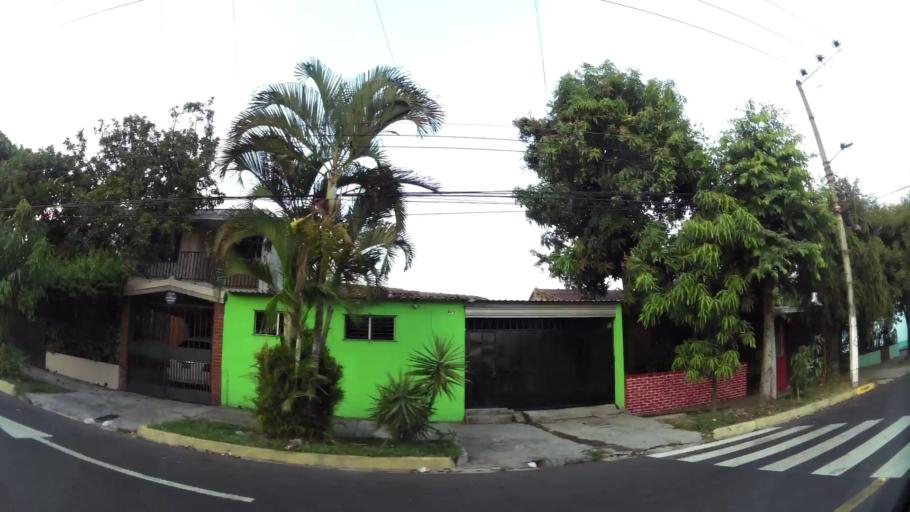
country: SV
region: San Salvador
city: Delgado
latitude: 13.7170
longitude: -89.1859
